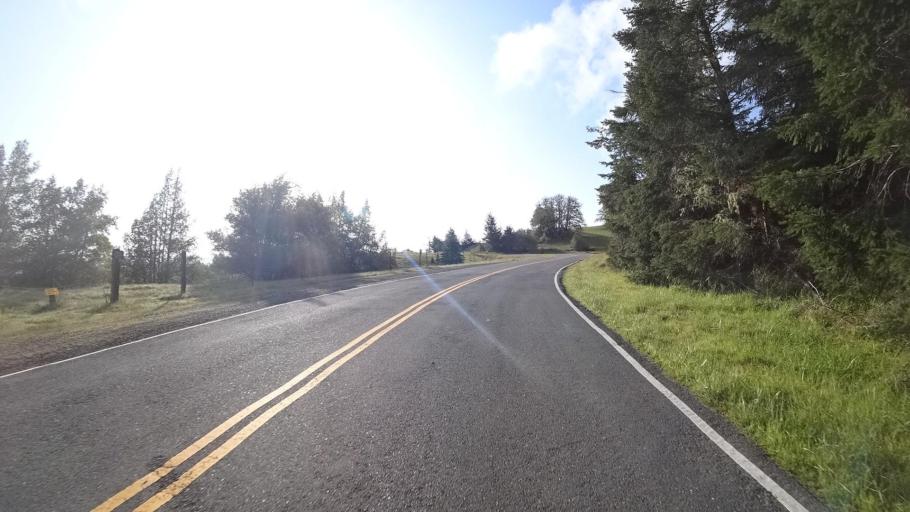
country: US
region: California
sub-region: Humboldt County
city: Blue Lake
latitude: 40.7388
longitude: -123.9502
